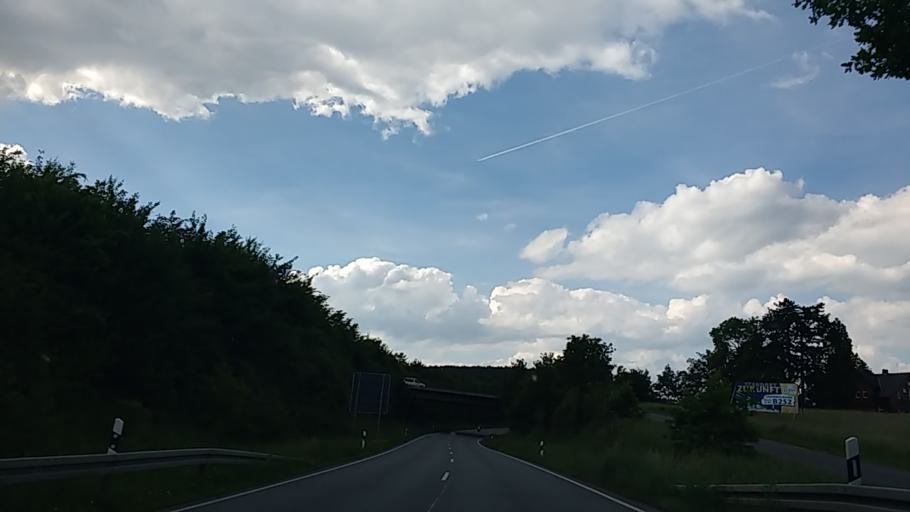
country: DE
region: Hesse
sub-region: Regierungsbezirk Kassel
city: Bad Arolsen
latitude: 51.3744
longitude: 8.9966
